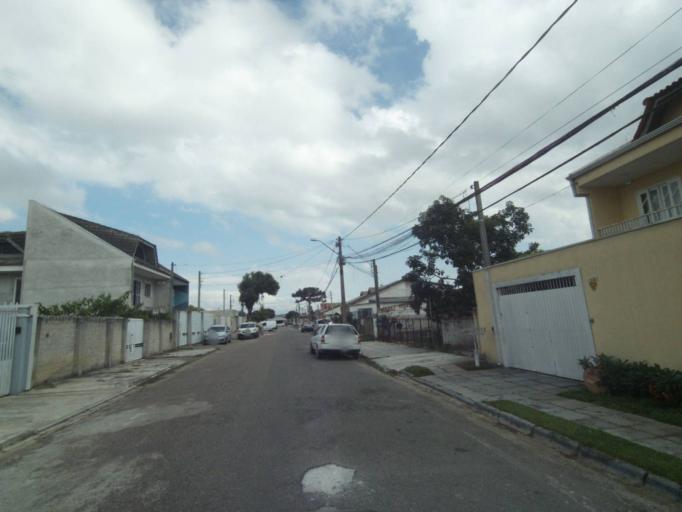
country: BR
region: Parana
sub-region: Pinhais
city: Pinhais
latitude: -25.4484
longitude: -49.2056
